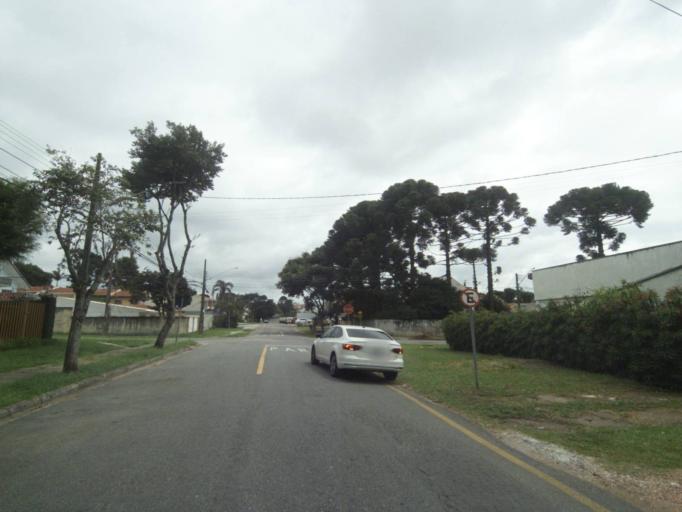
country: BR
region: Parana
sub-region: Pinhais
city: Pinhais
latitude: -25.4566
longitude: -49.2208
